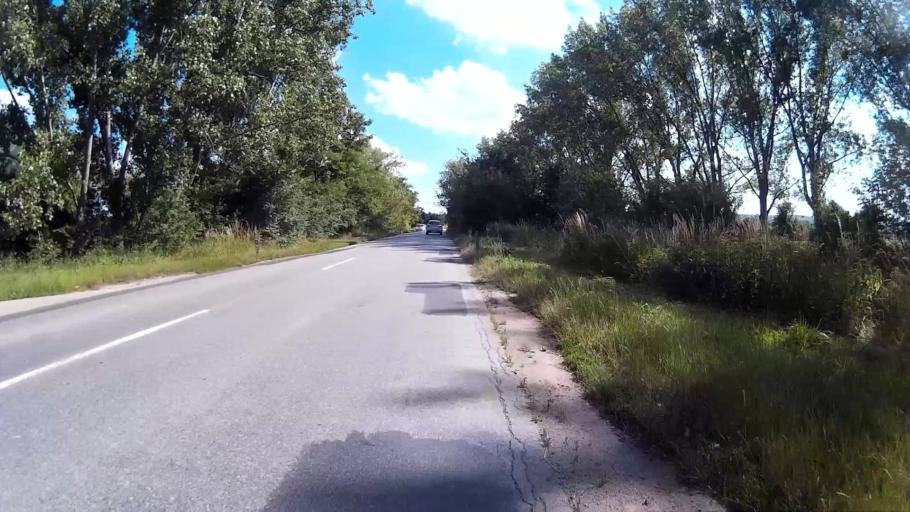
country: CZ
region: South Moravian
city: Menin
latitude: 49.0736
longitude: 16.6931
